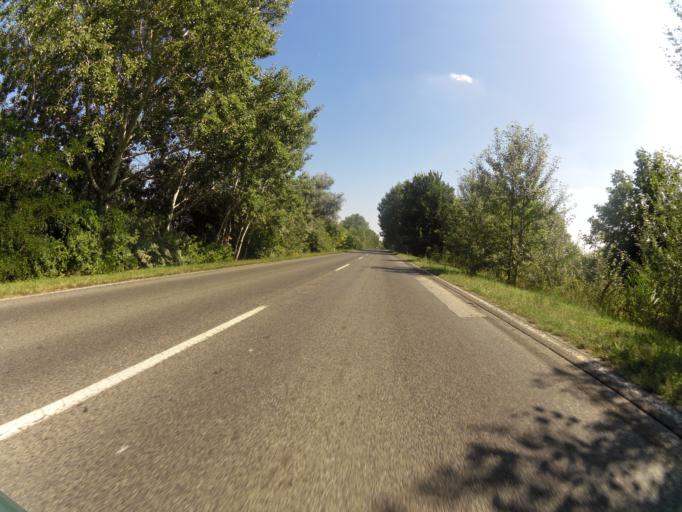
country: HU
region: Csongrad
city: Szatymaz
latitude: 46.3454
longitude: 20.0629
